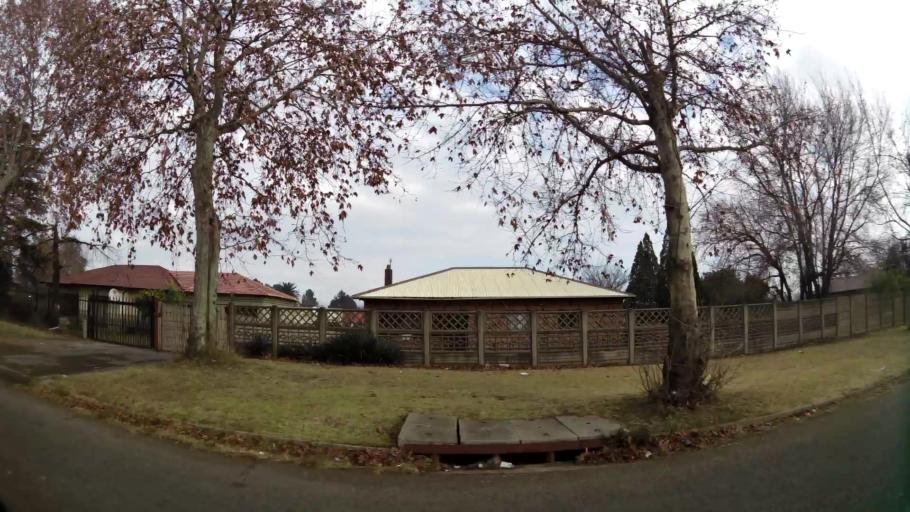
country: ZA
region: Gauteng
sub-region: Sedibeng District Municipality
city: Vanderbijlpark
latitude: -26.6867
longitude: 27.8155
